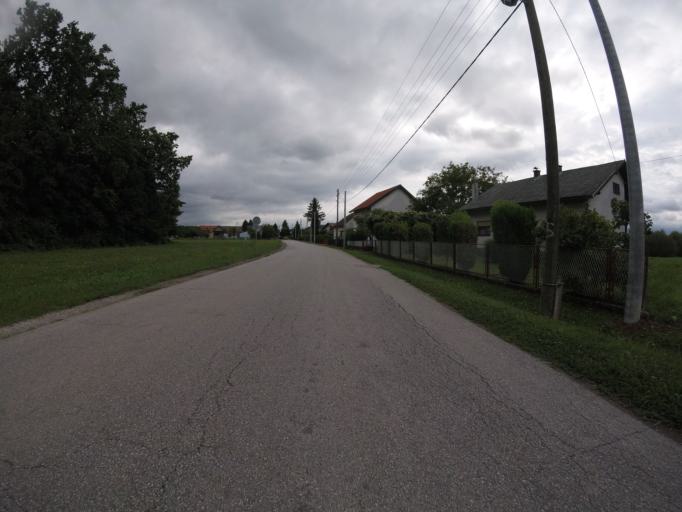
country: HR
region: Zagrebacka
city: Gradici
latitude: 45.6949
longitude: 16.0337
